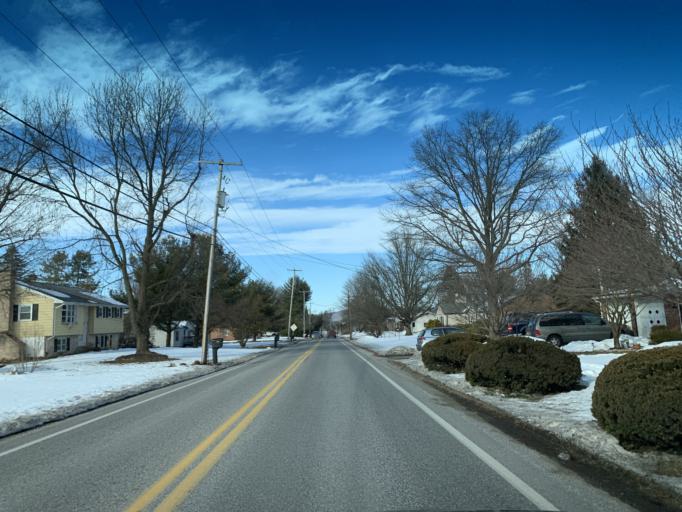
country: US
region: Pennsylvania
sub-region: York County
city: Dover
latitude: 39.9746
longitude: -76.8496
